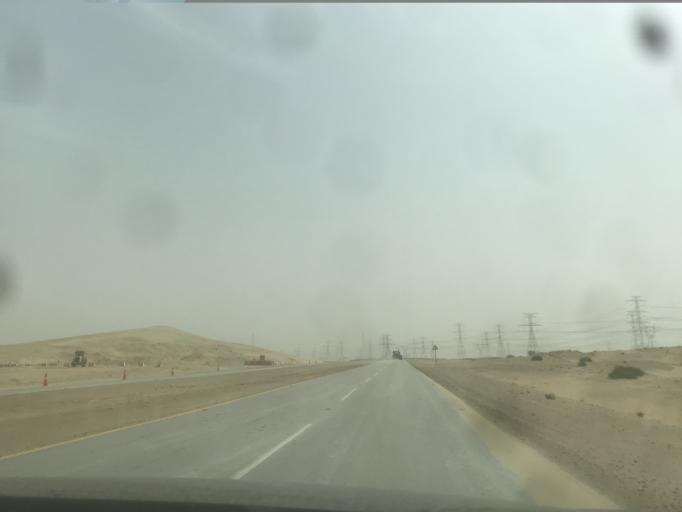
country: SA
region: Eastern Province
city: Abqaiq
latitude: 25.9093
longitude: 49.8852
